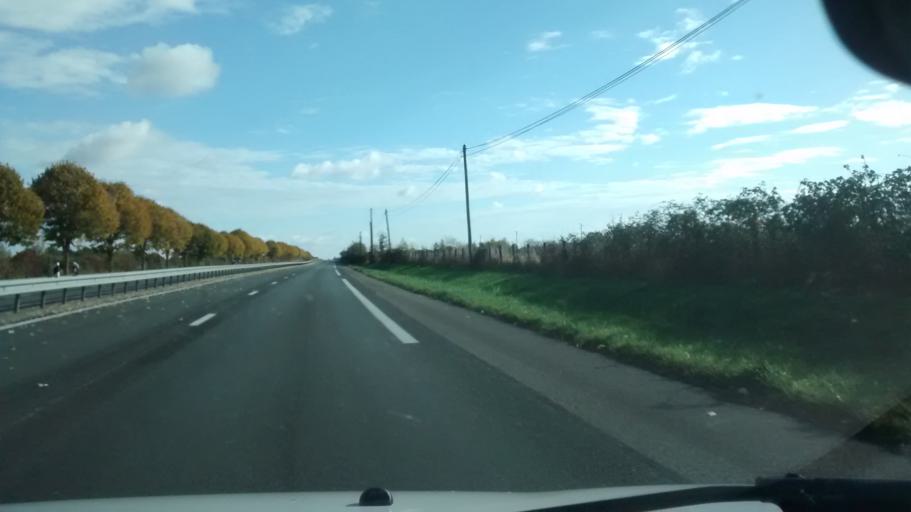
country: FR
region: Pays de la Loire
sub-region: Departement de Maine-et-Loire
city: Pouance
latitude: 47.7340
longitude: -1.1345
